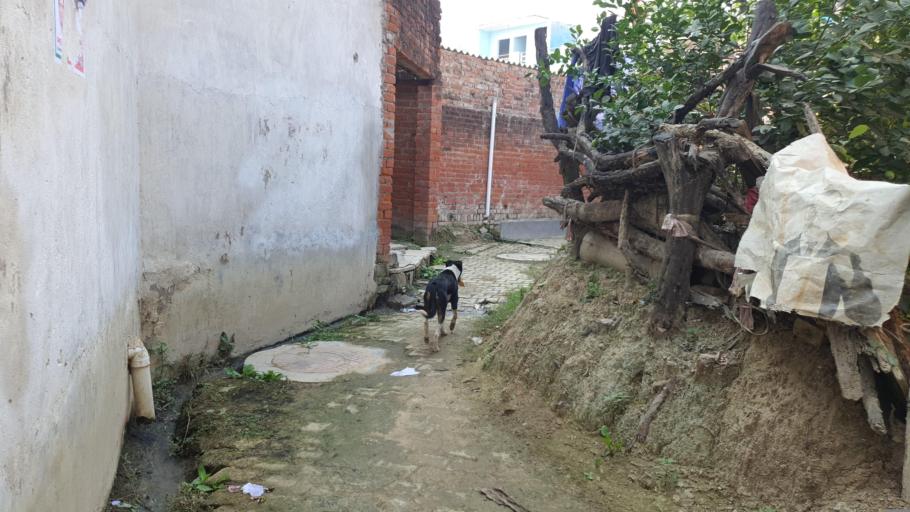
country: IN
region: Uttar Pradesh
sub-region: Lucknow District
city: Goshainganj
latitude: 26.7724
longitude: 81.0113
